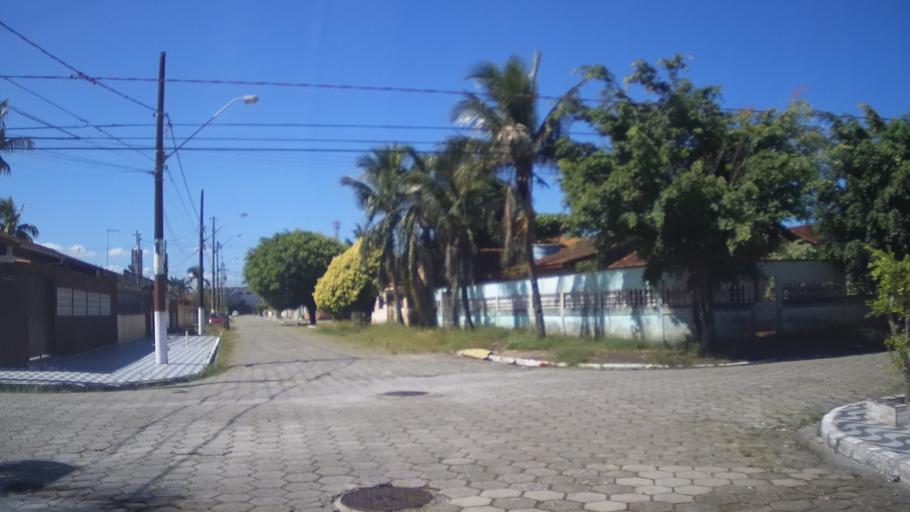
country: BR
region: Sao Paulo
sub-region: Praia Grande
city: Praia Grande
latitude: -24.0383
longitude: -46.5069
